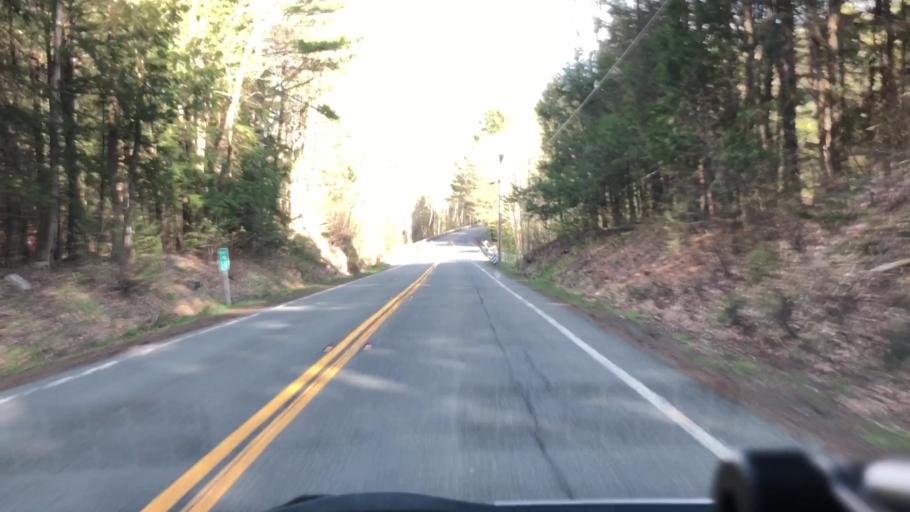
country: US
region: Massachusetts
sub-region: Hampshire County
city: Chesterfield
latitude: 42.3482
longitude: -72.8993
